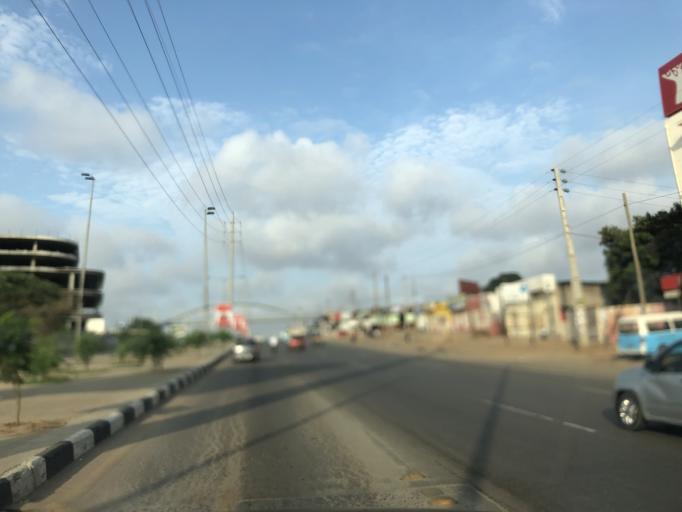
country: AO
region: Luanda
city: Luanda
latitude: -8.8947
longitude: 13.2297
